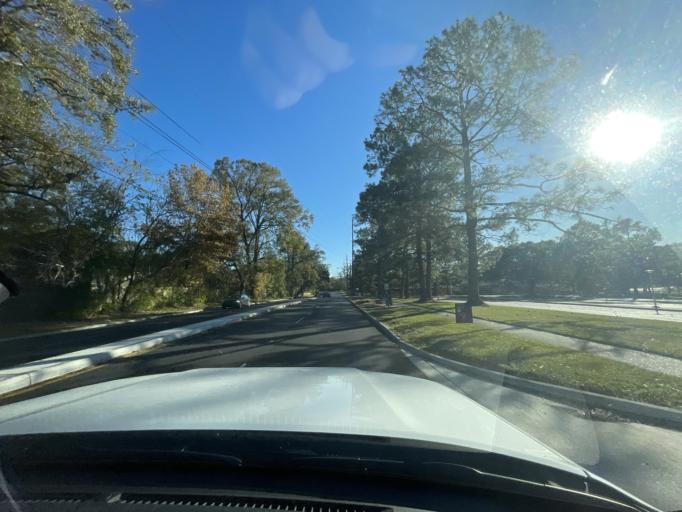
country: US
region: Louisiana
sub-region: East Baton Rouge Parish
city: Baton Rouge
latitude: 30.4312
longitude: -91.1528
